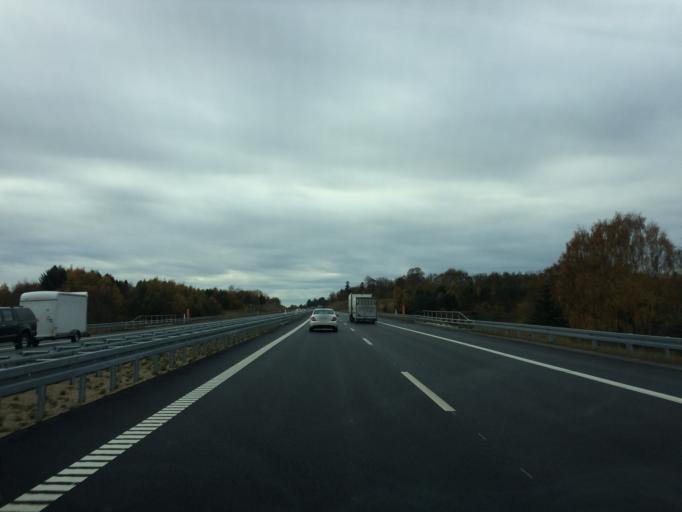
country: DK
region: Central Jutland
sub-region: Silkeborg Kommune
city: Silkeborg
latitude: 56.1824
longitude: 9.4854
